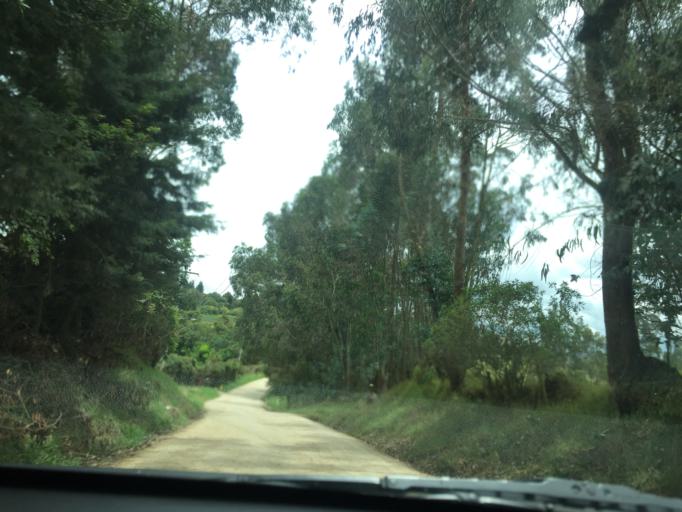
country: CO
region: Cundinamarca
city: El Rosal
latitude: 4.8692
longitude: -74.2552
